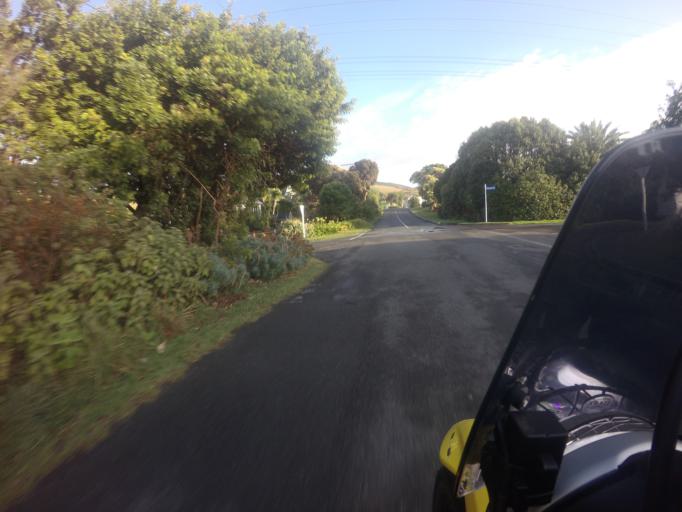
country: NZ
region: Gisborne
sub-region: Gisborne District
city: Gisborne
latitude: -38.6762
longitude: 178.0806
